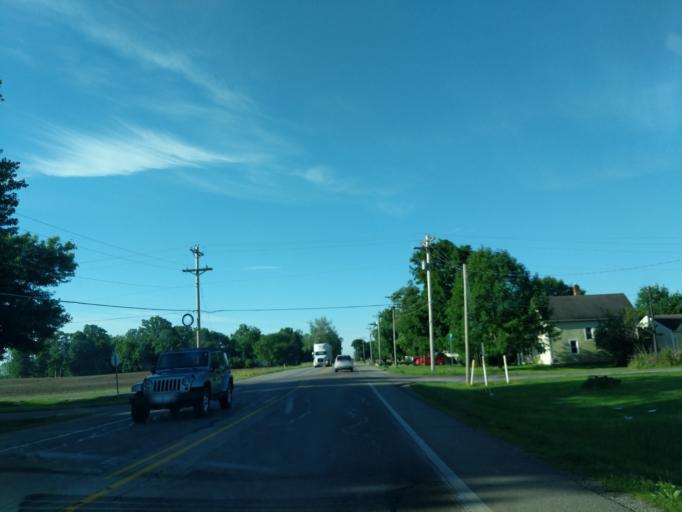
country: US
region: Indiana
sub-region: Hancock County
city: Greenfield
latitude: 39.8435
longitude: -85.7700
